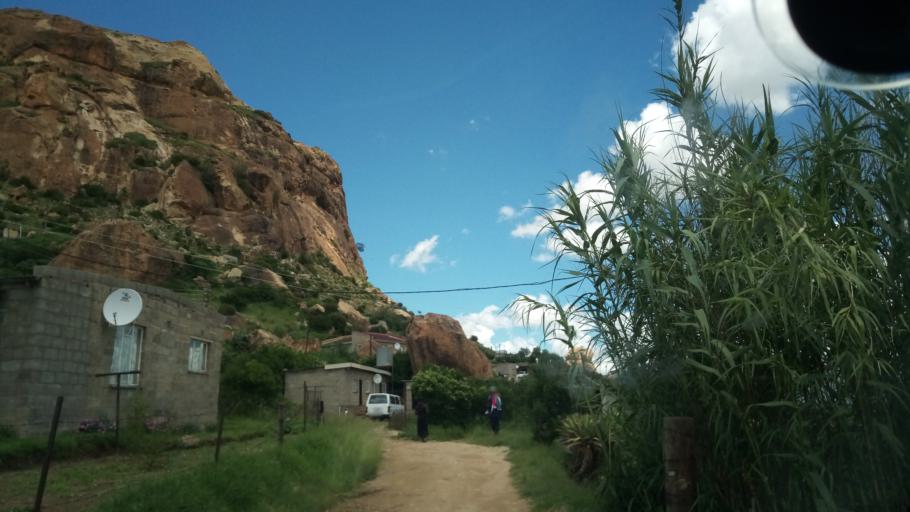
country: LS
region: Maseru
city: Maseru
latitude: -29.3511
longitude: 27.5334
